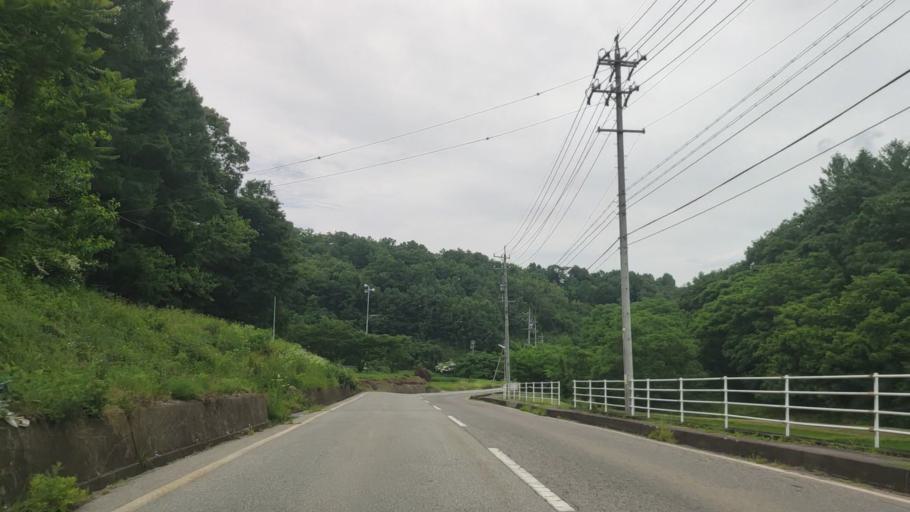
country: JP
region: Nagano
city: Kamimaruko
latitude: 36.3043
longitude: 138.3243
